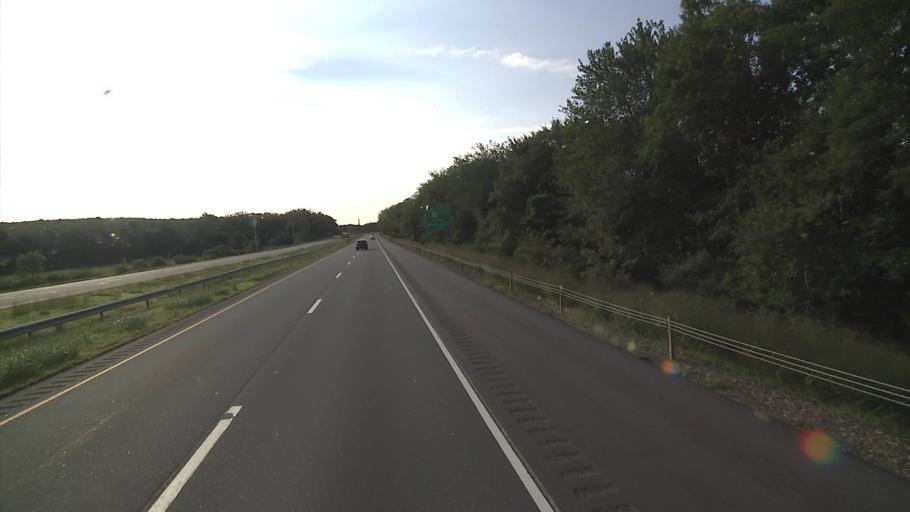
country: US
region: Connecticut
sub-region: New London County
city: Norwich
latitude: 41.5649
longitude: -72.1356
